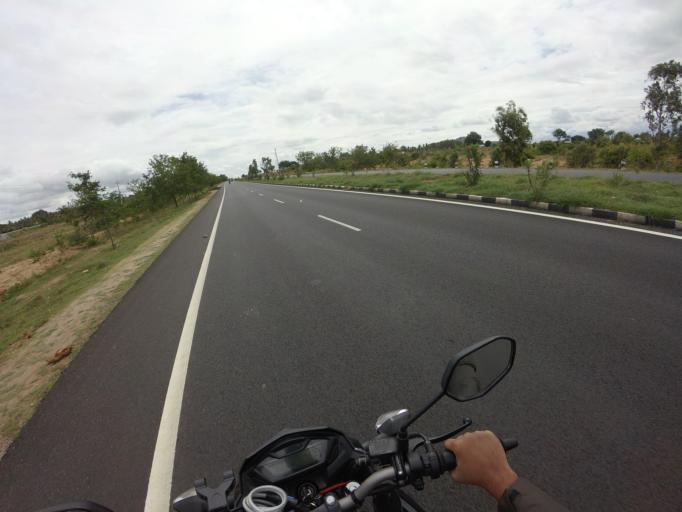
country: IN
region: Karnataka
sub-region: Mandya
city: Belluru
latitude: 12.9726
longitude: 76.8194
